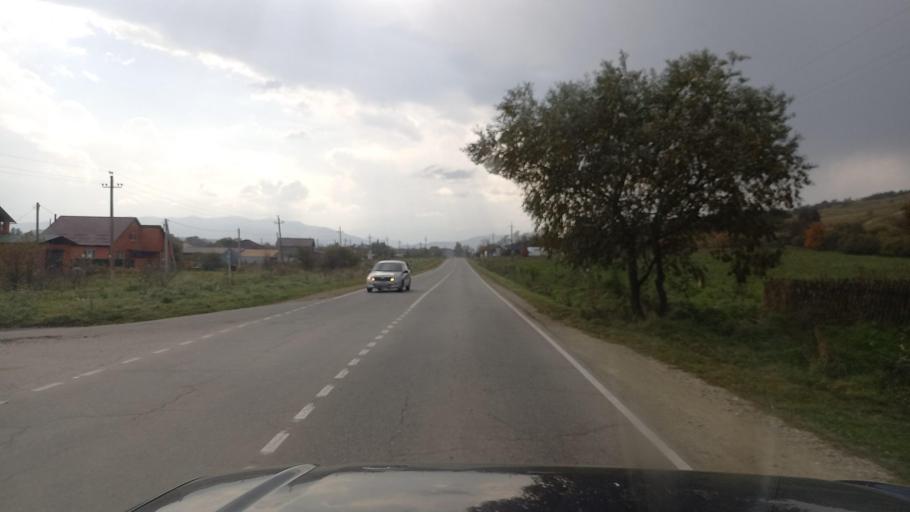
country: RU
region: Krasnodarskiy
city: Psebay
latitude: 44.1457
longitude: 40.8260
